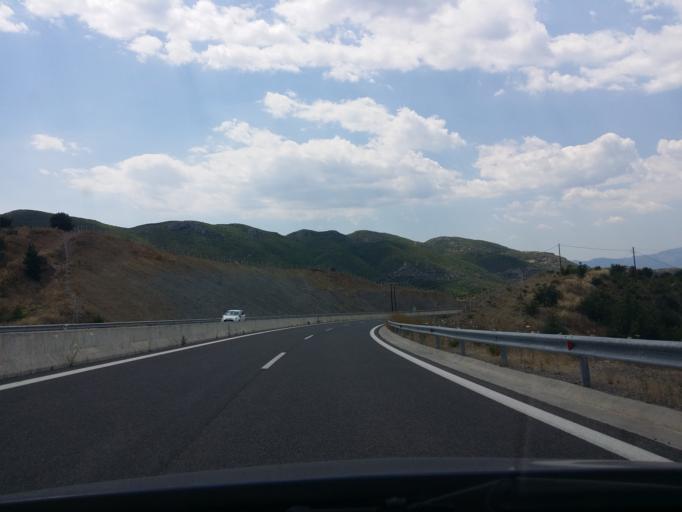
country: GR
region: Peloponnese
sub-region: Nomos Arkadias
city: Megalopoli
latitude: 37.3100
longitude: 22.1737
